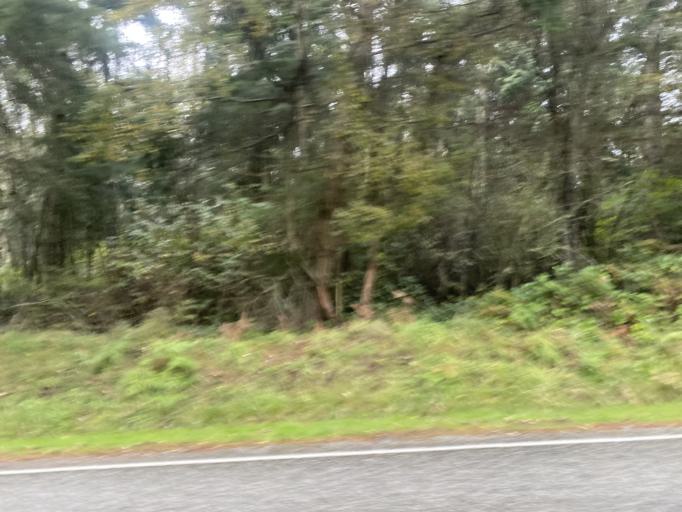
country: US
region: Washington
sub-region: Island County
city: Camano
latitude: 48.0934
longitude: -122.5069
